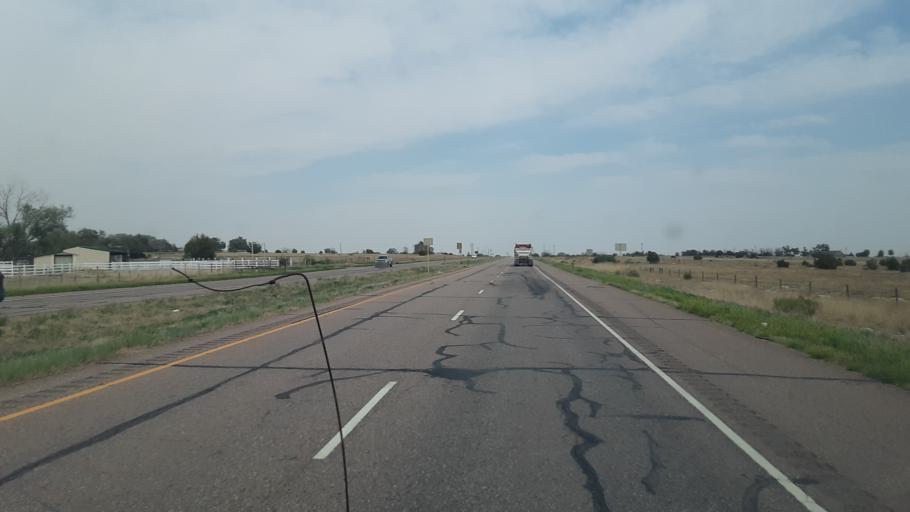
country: US
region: Colorado
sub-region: Fremont County
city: Penrose
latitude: 38.4095
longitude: -105.0078
